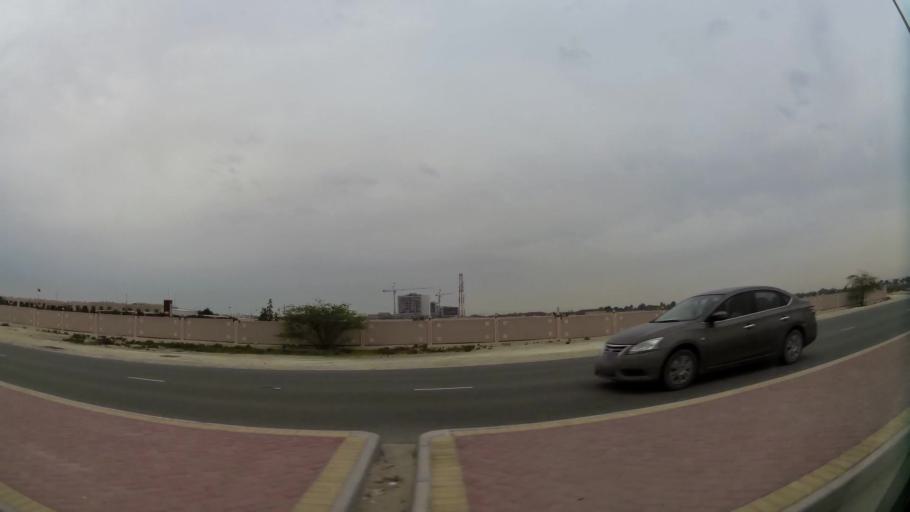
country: BH
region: Northern
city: Ar Rifa'
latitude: 26.0976
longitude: 50.5557
